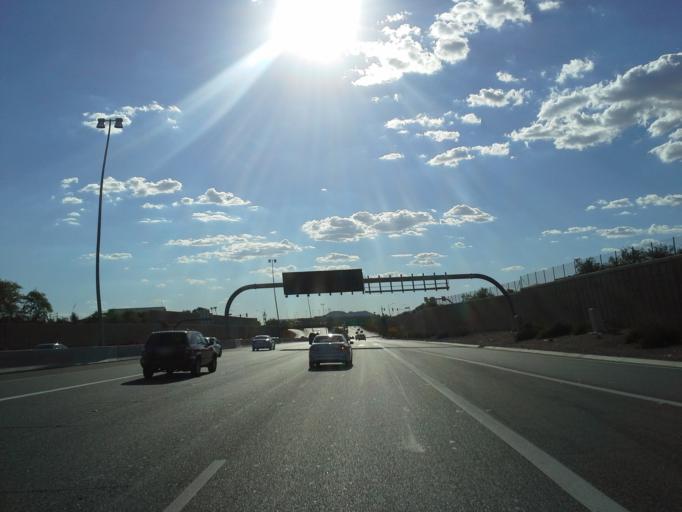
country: US
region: Arizona
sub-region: Maricopa County
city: Glendale
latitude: 33.6692
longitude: -112.0876
